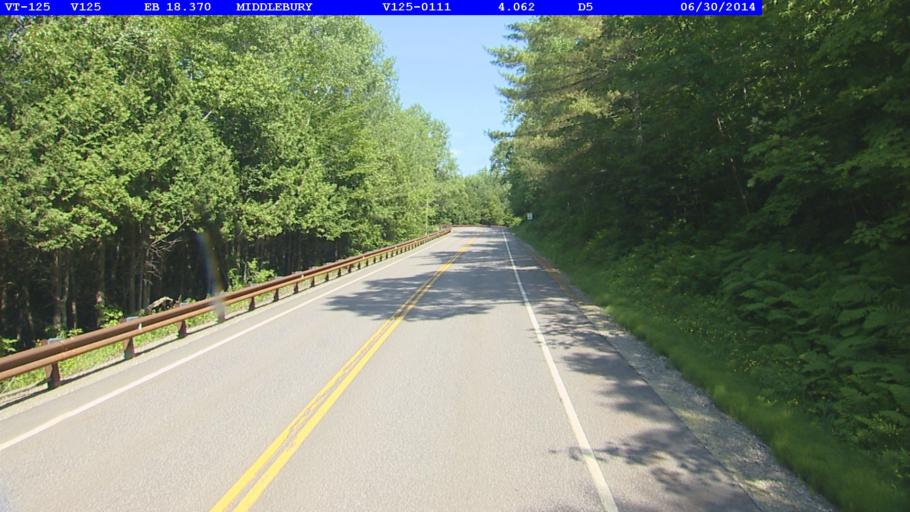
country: US
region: Vermont
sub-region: Addison County
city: Middlebury (village)
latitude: 43.9744
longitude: -73.0633
